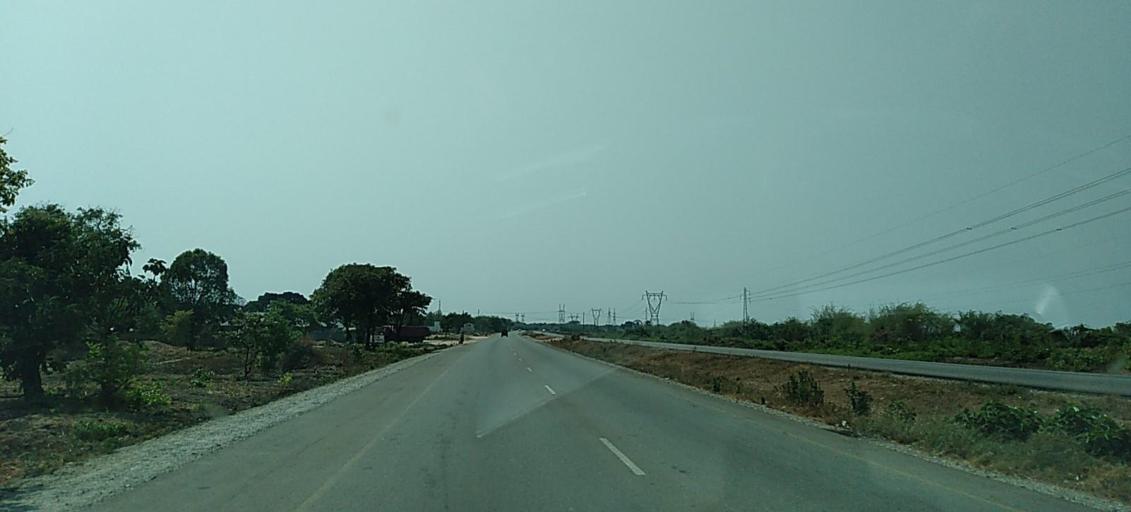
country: ZM
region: Copperbelt
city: Chambishi
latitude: -12.6044
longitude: 27.9708
